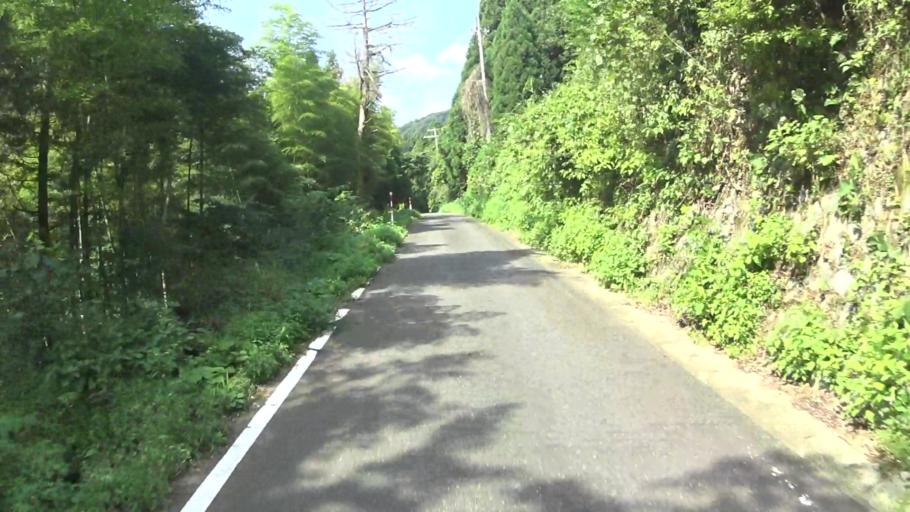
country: JP
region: Kyoto
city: Miyazu
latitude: 35.6557
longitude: 135.2525
